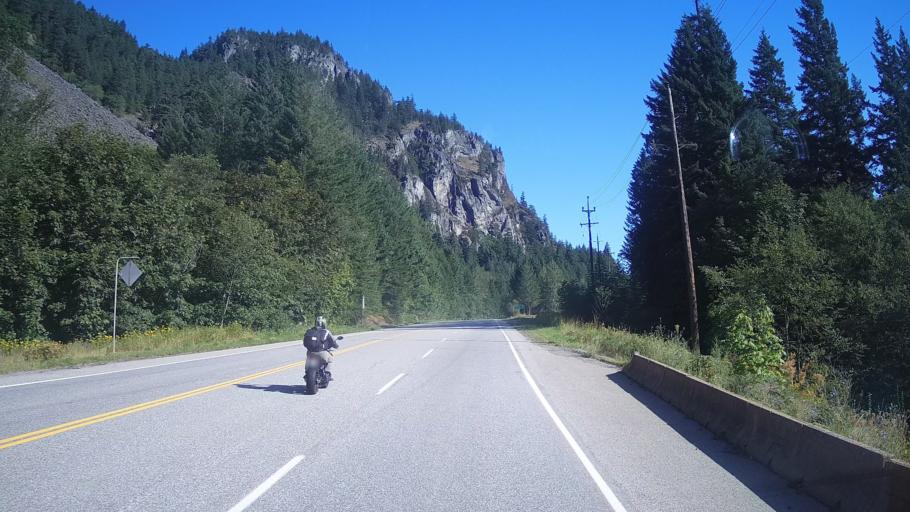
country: CA
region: British Columbia
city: Hope
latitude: 49.6422
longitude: -121.4102
